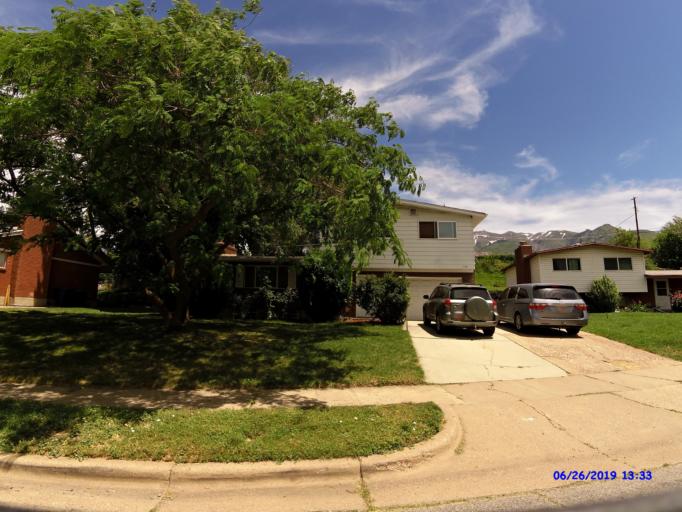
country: US
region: Utah
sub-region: Weber County
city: South Ogden
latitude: 41.2033
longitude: -111.9616
